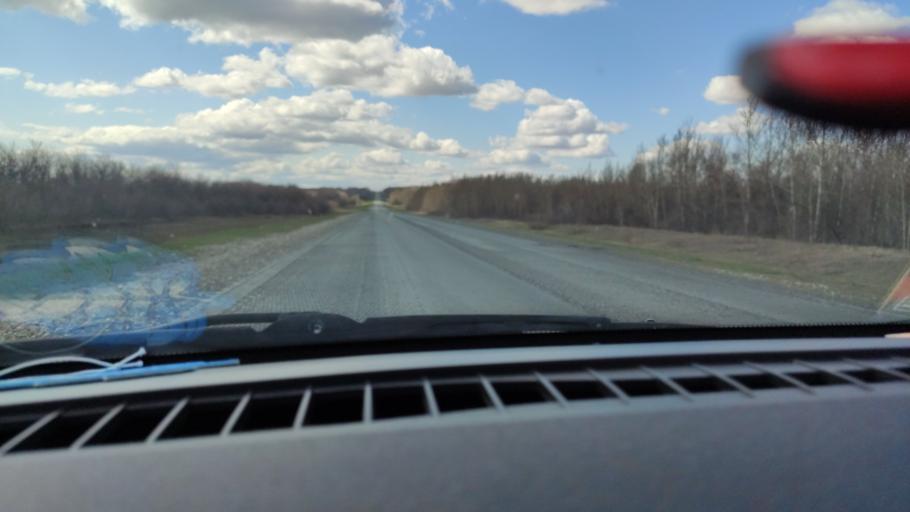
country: RU
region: Saratov
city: Dukhovnitskoye
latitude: 52.6953
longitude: 48.2486
